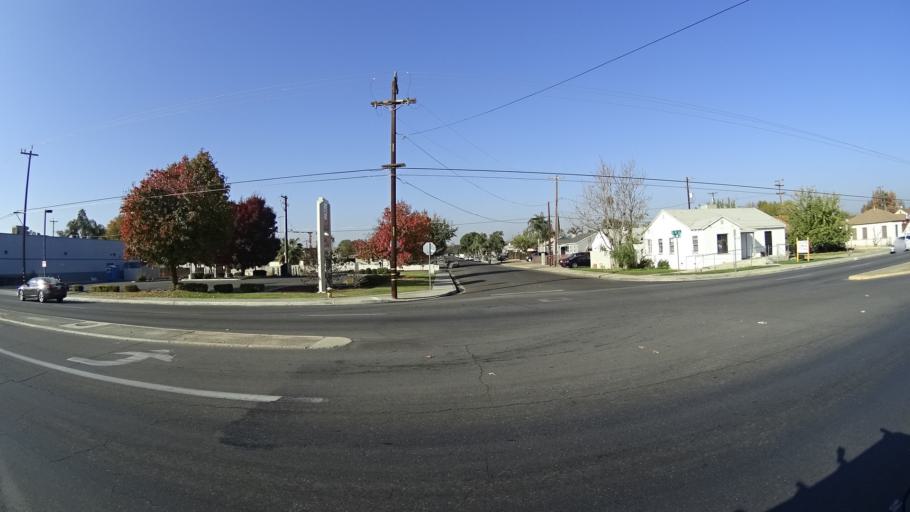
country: US
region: California
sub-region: Kern County
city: Bakersfield
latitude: 35.3411
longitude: -119.0212
